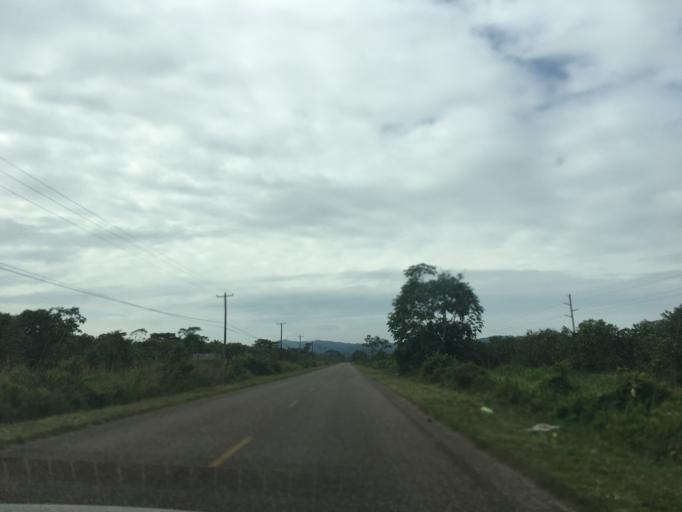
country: BZ
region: Stann Creek
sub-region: Dangriga
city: Dangriga
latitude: 16.8294
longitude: -88.3659
